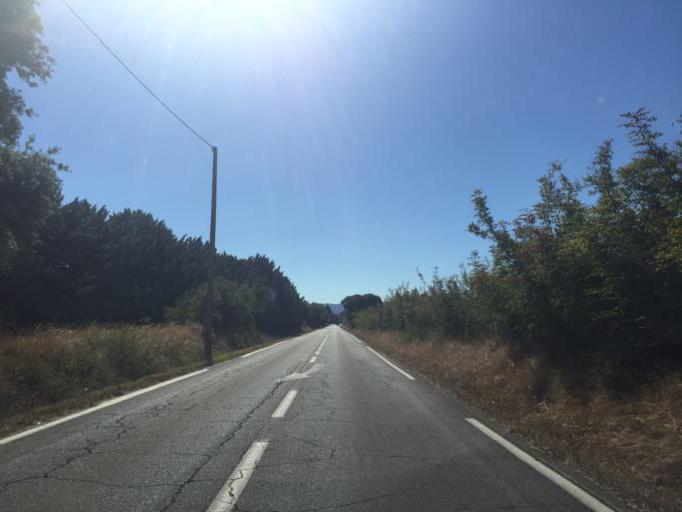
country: FR
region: Provence-Alpes-Cote d'Azur
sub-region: Departement du Vaucluse
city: Carpentras
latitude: 44.0317
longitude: 5.0798
